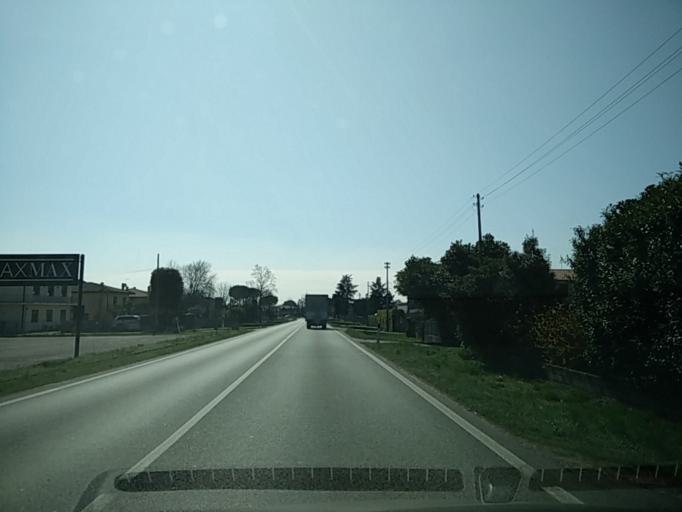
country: IT
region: Veneto
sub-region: Provincia di Treviso
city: Caerano di San Marco
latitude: 45.7660
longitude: 11.9946
